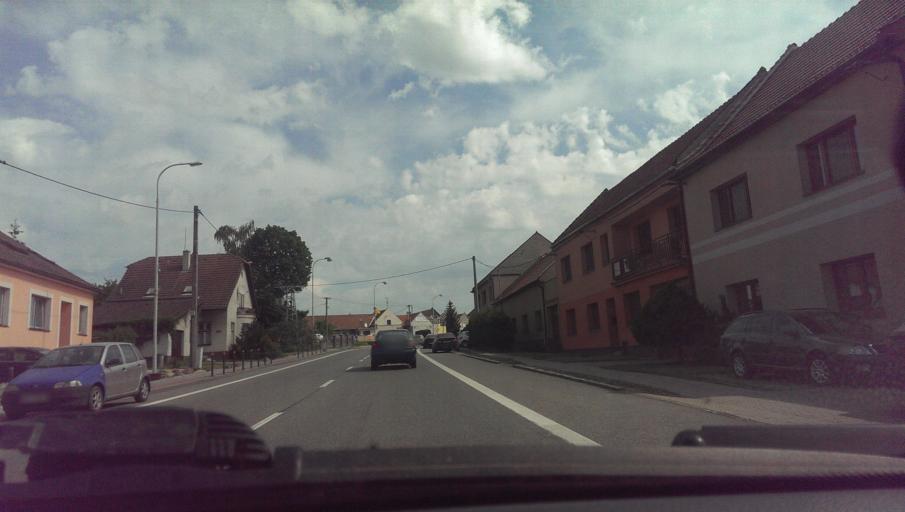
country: CZ
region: Zlin
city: Spytihnev
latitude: 49.1370
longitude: 17.4913
